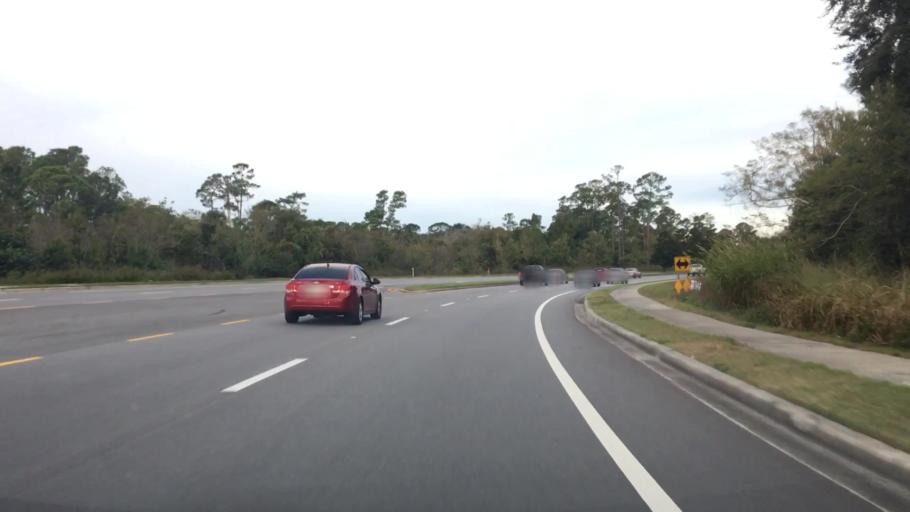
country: US
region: Florida
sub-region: Seminole County
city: Midway
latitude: 28.7568
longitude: -81.2390
